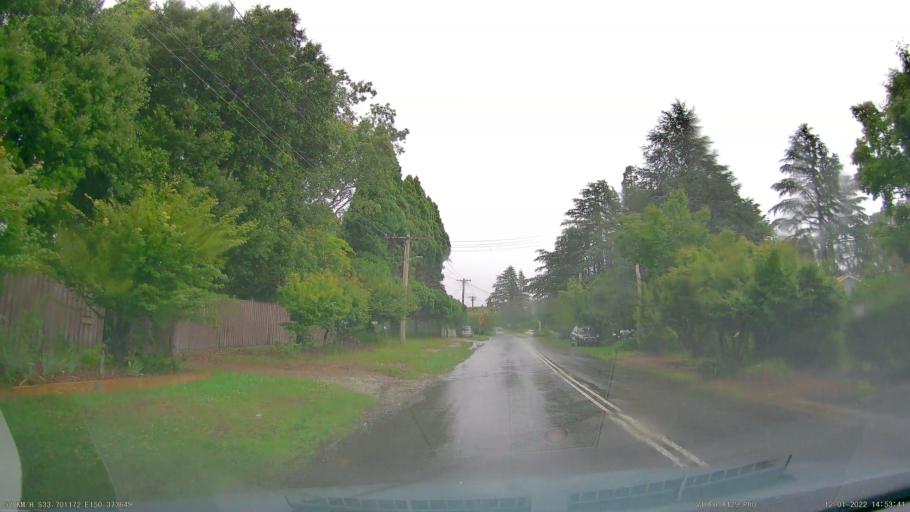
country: AU
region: New South Wales
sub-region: Blue Mountains Municipality
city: Leura
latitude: -33.7013
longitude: 150.3737
